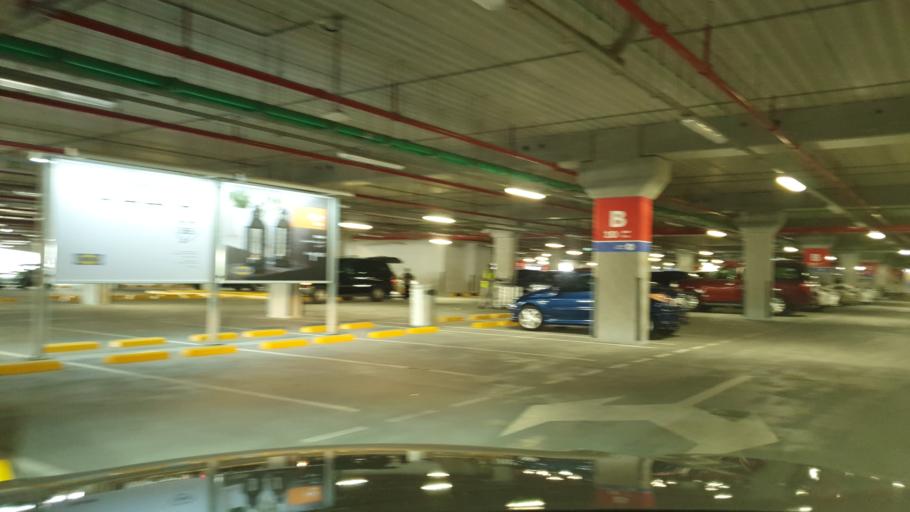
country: BH
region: Northern
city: Madinat `Isa
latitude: 26.1796
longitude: 50.5045
